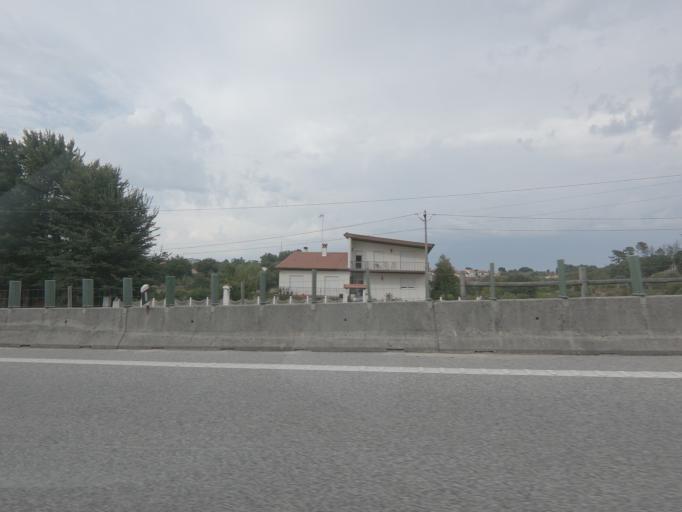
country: PT
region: Viseu
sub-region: Santa Comba Dao
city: Santa Comba Dao
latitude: 40.3857
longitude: -8.1204
